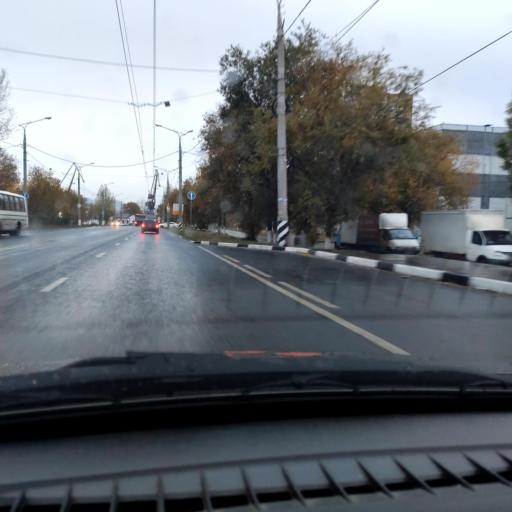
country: RU
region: Samara
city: Zhigulevsk
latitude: 53.4788
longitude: 49.4861
